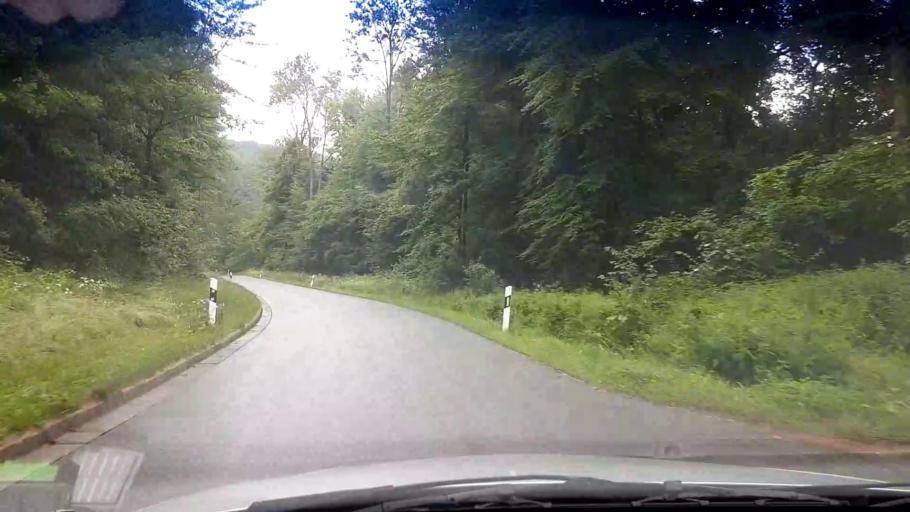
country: DE
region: Bavaria
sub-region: Upper Franconia
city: Altendorf
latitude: 50.0680
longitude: 11.1554
